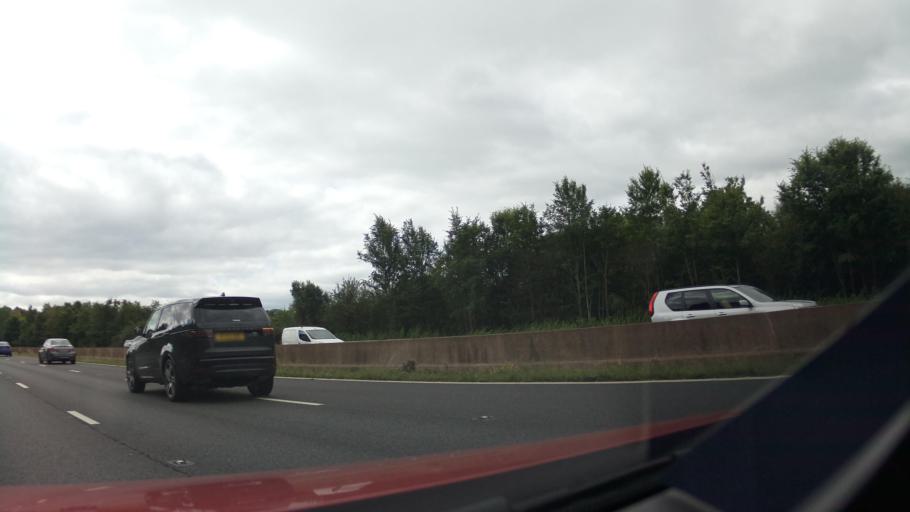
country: GB
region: England
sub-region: Devon
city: Cullompton
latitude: 50.8479
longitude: -3.3888
